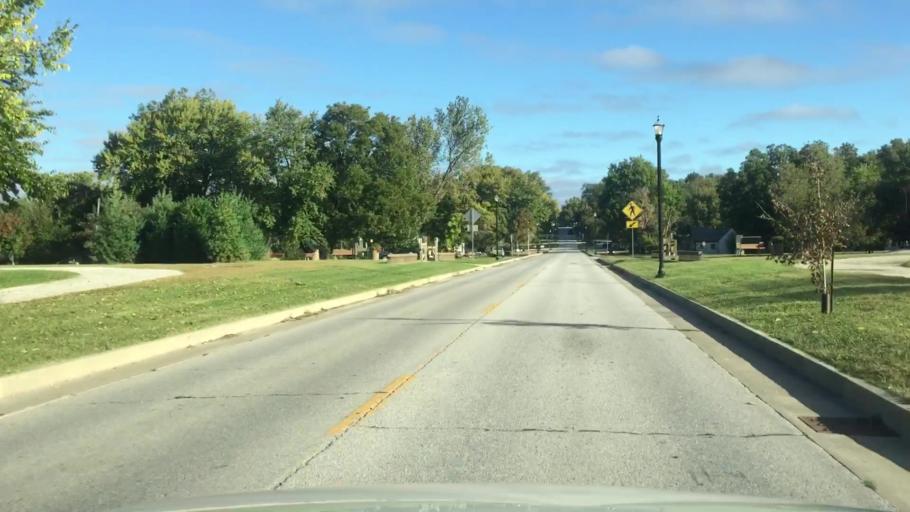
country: US
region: Missouri
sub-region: Howard County
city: New Franklin
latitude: 39.0120
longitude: -92.7377
